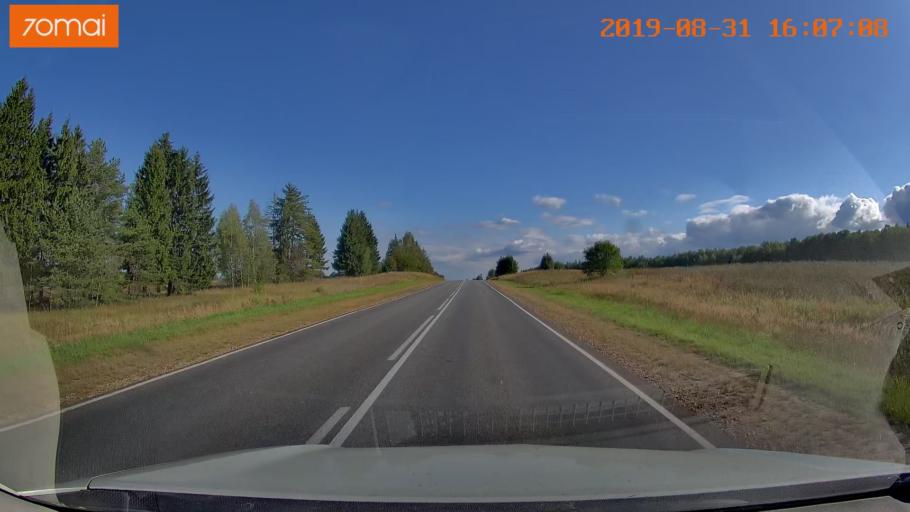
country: RU
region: Kaluga
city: Yukhnov
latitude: 54.6139
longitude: 35.3549
